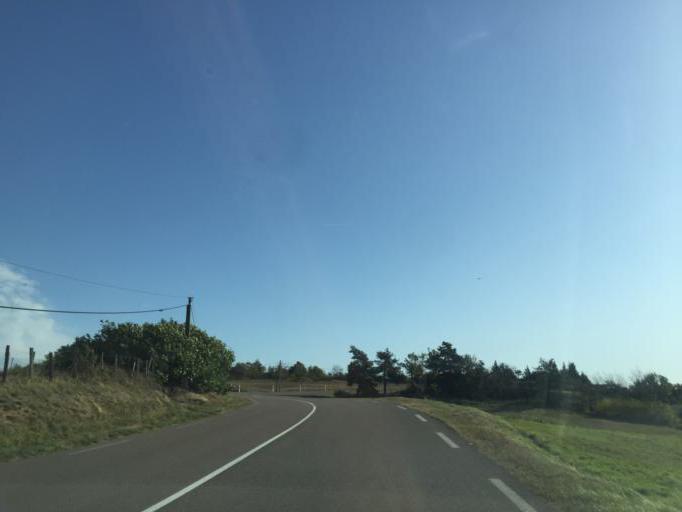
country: FR
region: Rhone-Alpes
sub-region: Departement de la Loire
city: Perigneux
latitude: 45.4597
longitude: 4.1091
